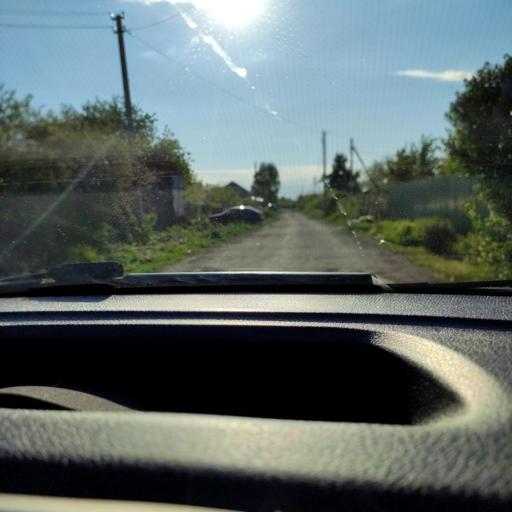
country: RU
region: Samara
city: Tol'yatti
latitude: 53.5836
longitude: 49.3002
